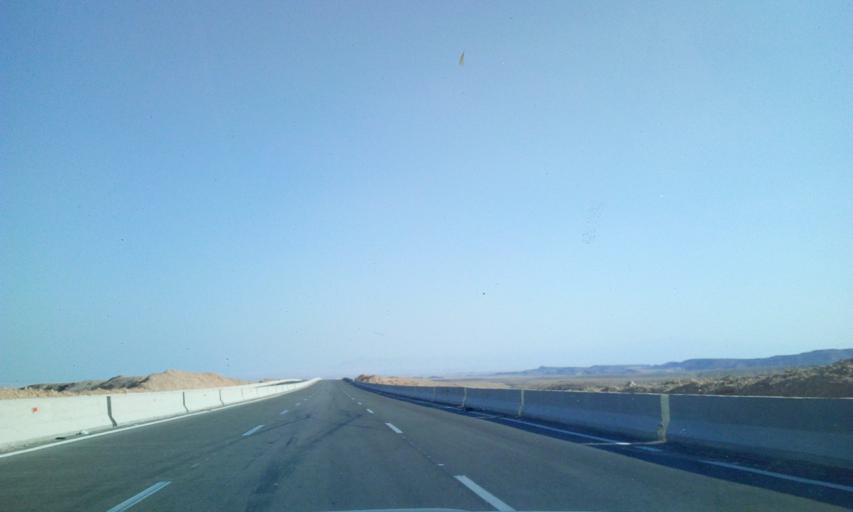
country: EG
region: As Suways
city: Ain Sukhna
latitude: 29.2638
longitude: 32.4730
